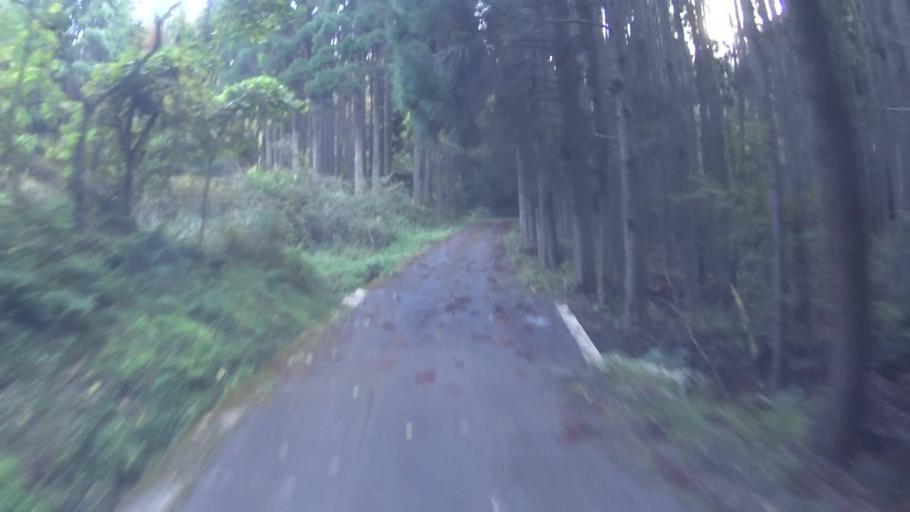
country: JP
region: Kyoto
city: Ayabe
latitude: 35.2708
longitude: 135.2488
